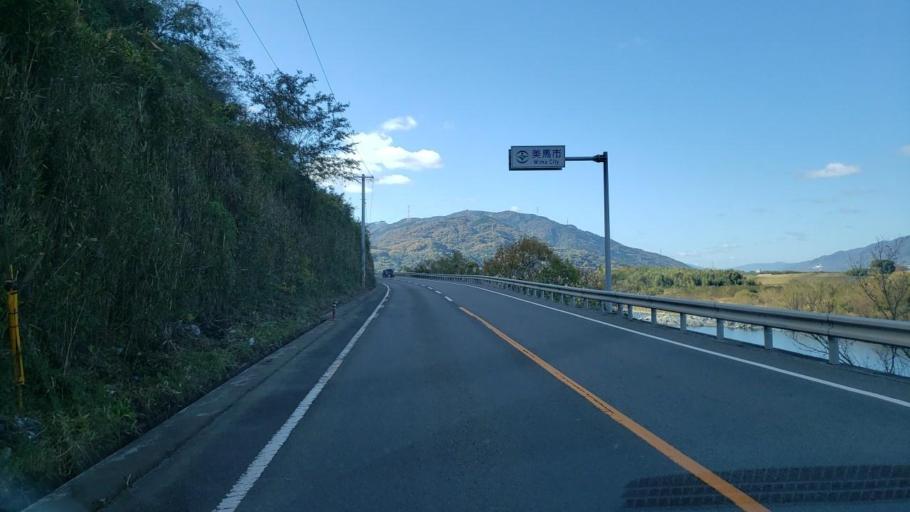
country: JP
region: Tokushima
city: Wakimachi
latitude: 34.0620
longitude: 134.1889
